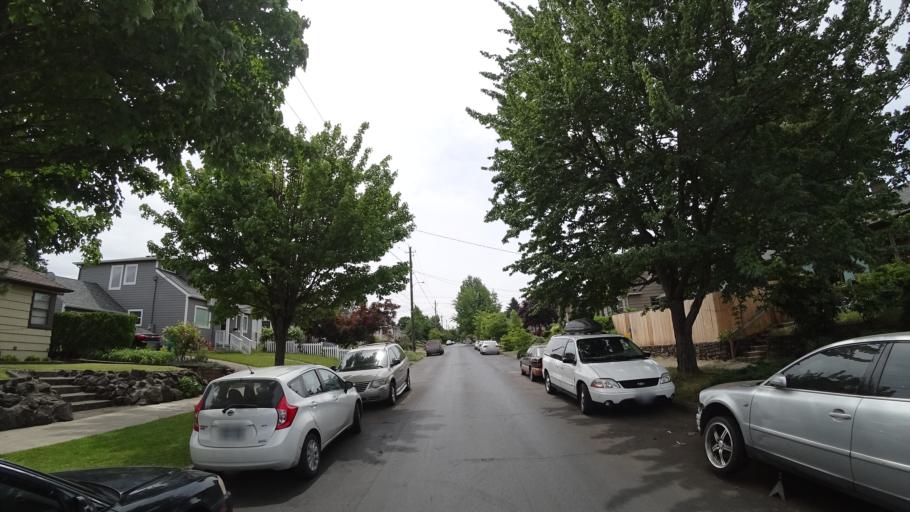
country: US
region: Oregon
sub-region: Multnomah County
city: Portland
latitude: 45.5626
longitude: -122.6287
